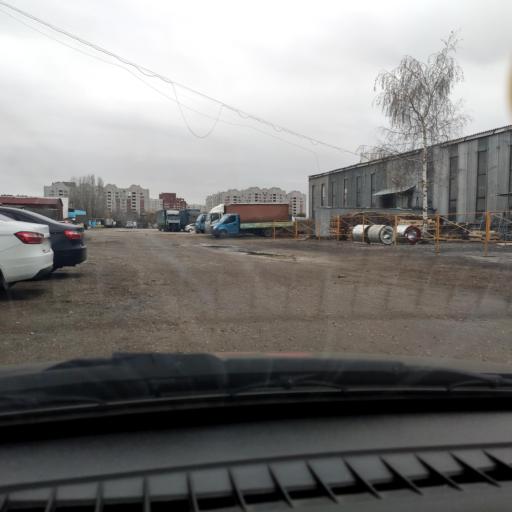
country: RU
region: Samara
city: Tol'yatti
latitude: 53.5535
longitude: 49.3271
